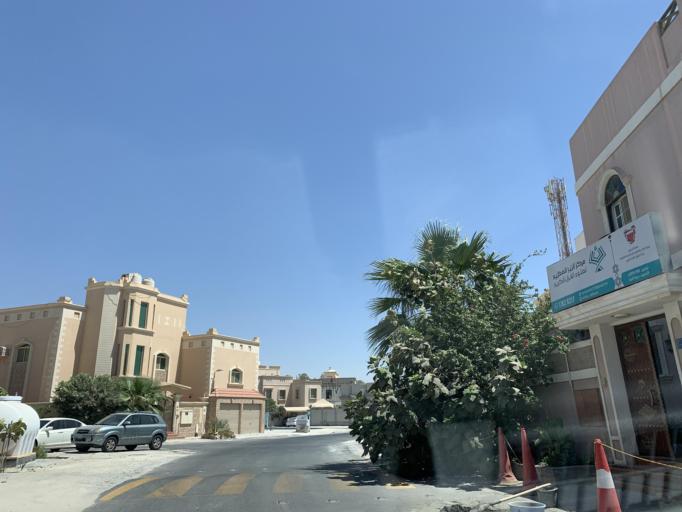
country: BH
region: Manama
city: Jidd Hafs
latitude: 26.2313
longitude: 50.4867
